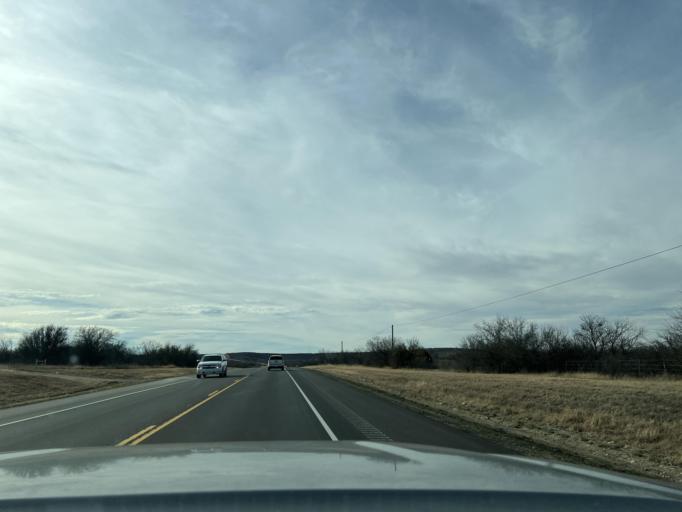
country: US
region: Texas
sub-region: Shackelford County
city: Albany
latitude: 32.7136
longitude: -99.3442
